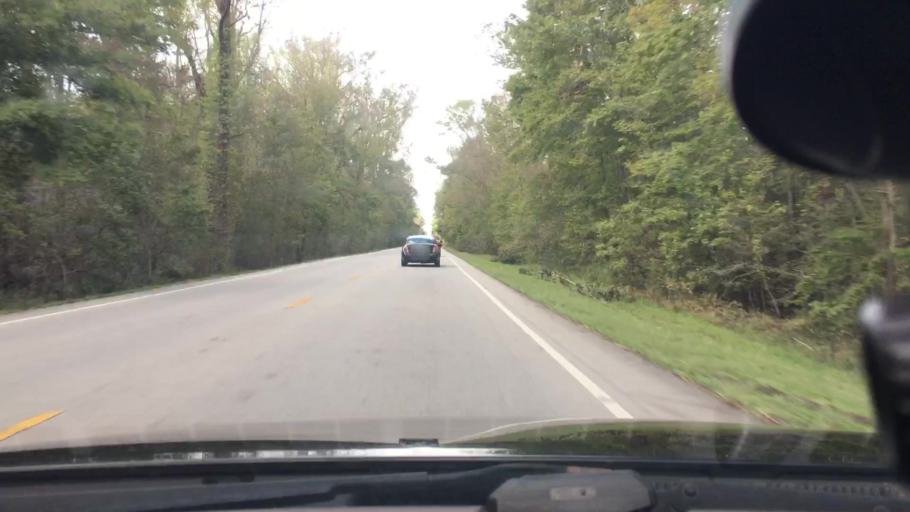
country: US
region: North Carolina
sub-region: Craven County
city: New Bern
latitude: 35.1876
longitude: -77.0507
